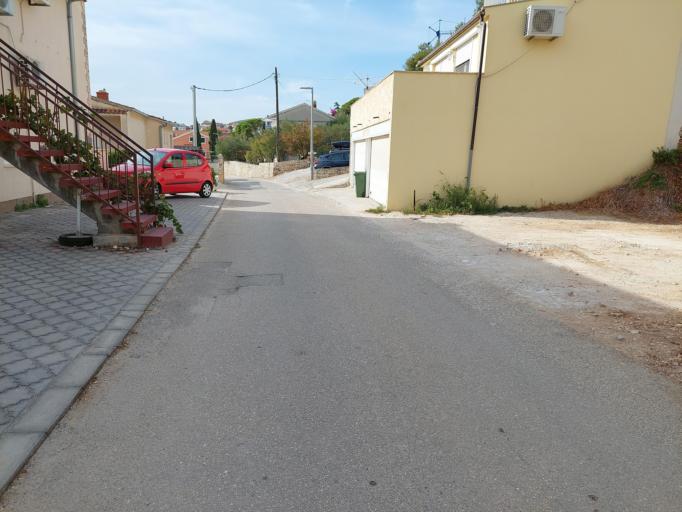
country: HR
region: Splitsko-Dalmatinska
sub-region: Grad Trogir
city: Trogir
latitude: 43.4916
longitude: 16.2776
